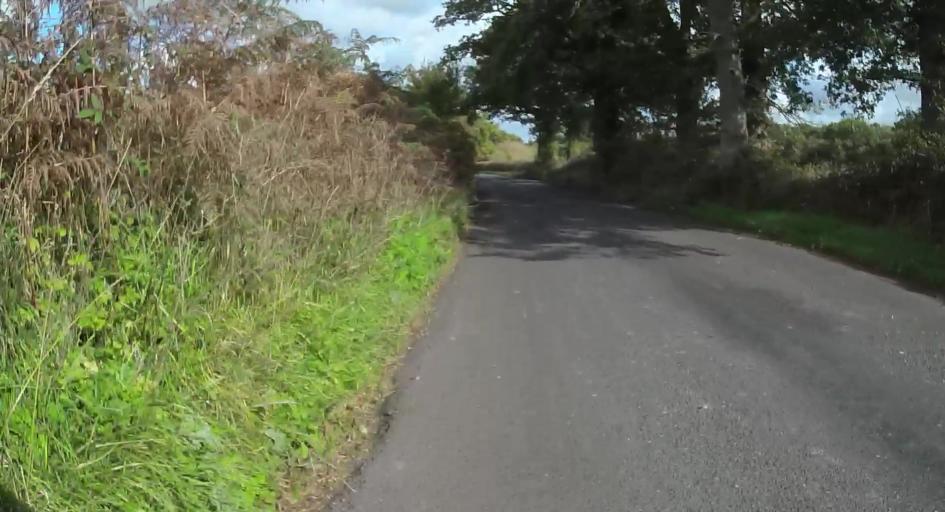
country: GB
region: England
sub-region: Hampshire
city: Fleet
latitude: 51.2839
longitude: -0.8782
